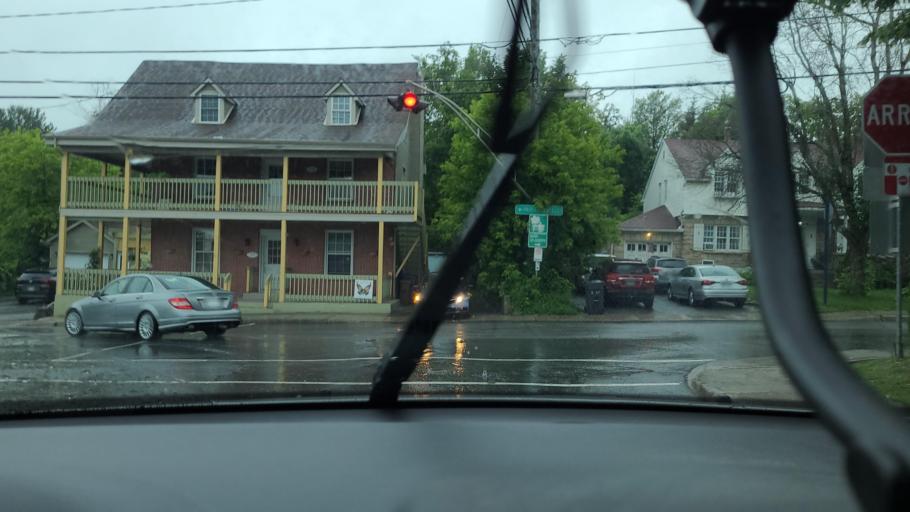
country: CA
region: Quebec
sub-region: Outaouais
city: Saint-Andre-Avellin
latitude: 45.7215
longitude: -75.0572
